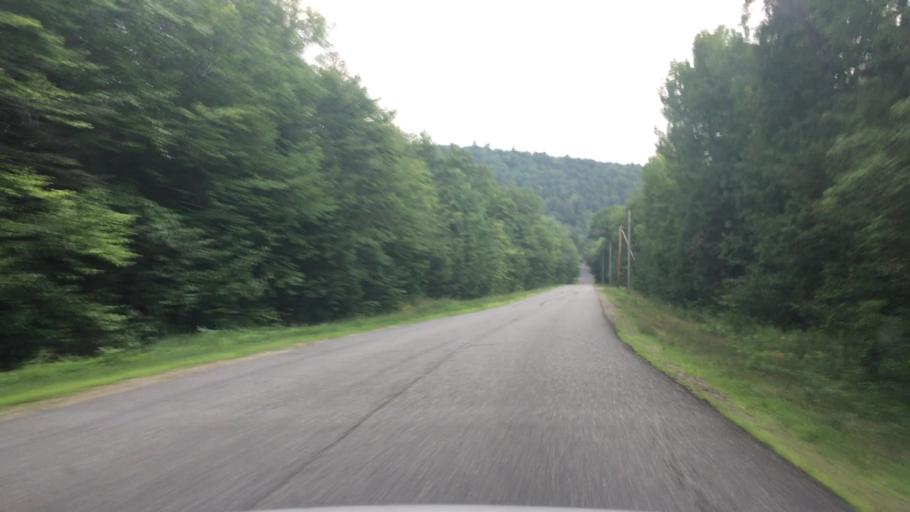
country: US
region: Maine
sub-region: Knox County
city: Washington
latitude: 44.3701
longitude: -69.3454
